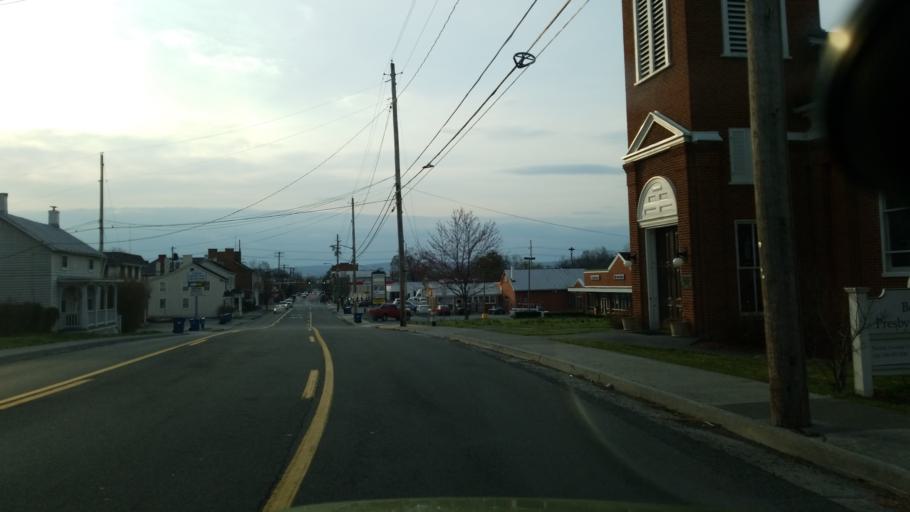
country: US
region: Virginia
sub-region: Clarke County
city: Berryville
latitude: 39.1526
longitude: -77.9843
